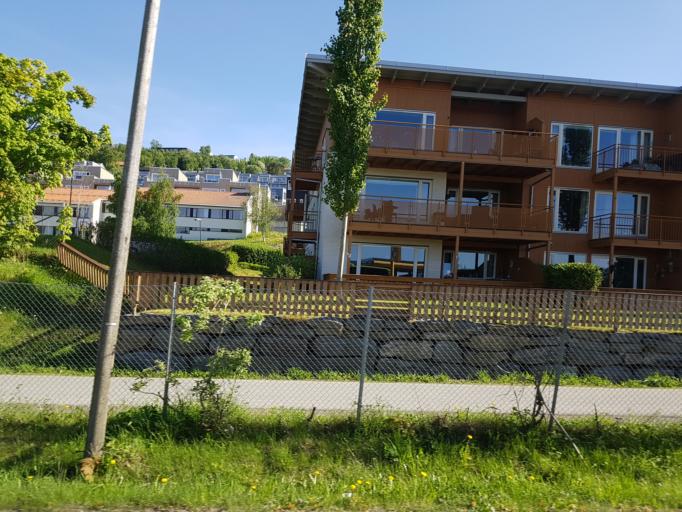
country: NO
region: Sor-Trondelag
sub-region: Malvik
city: Malvik
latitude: 63.4402
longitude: 10.6390
